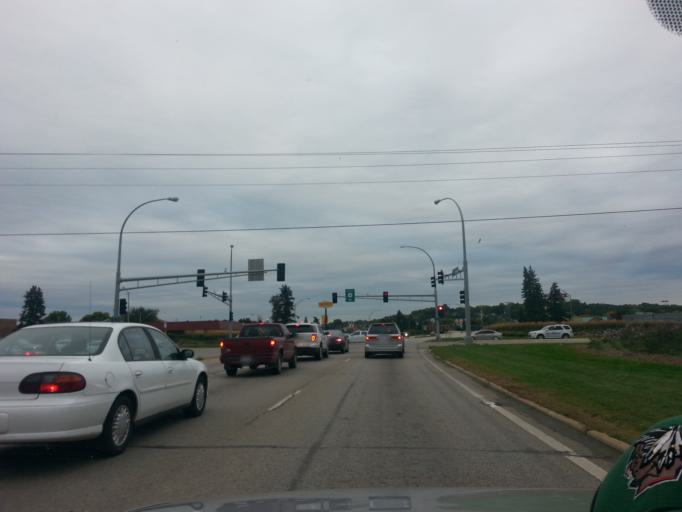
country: US
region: Minnesota
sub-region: Olmsted County
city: Rochester
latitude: 44.0075
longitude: -92.4632
